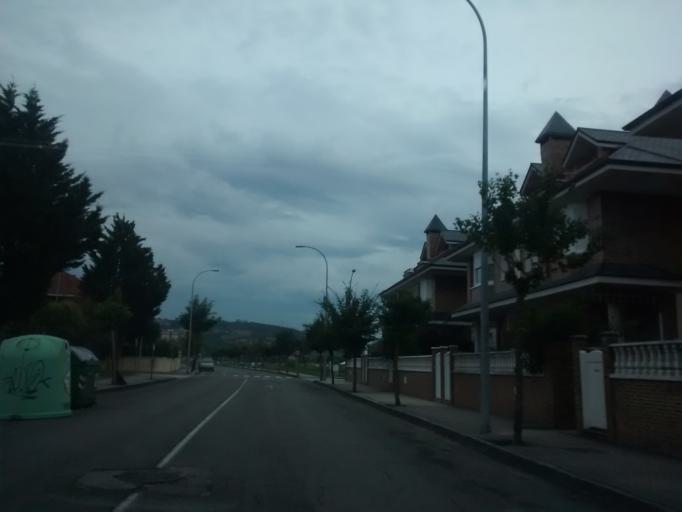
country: ES
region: Cantabria
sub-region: Provincia de Cantabria
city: Colindres
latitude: 43.4206
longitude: -3.4474
